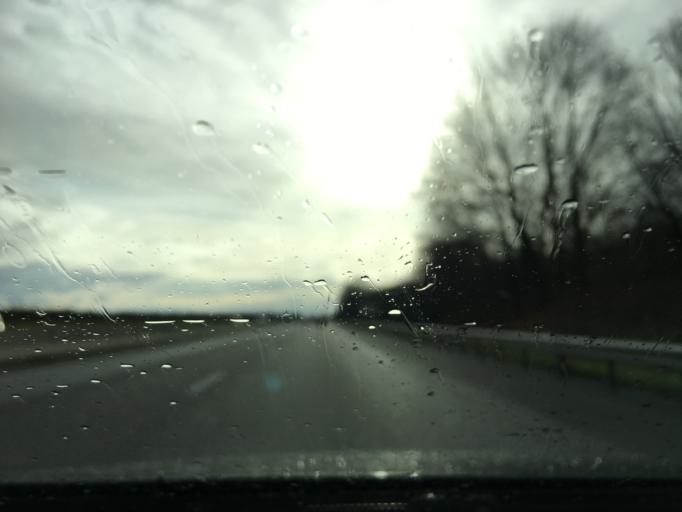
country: FR
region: Alsace
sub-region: Departement du Haut-Rhin
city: Rixheim
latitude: 47.7534
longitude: 7.4200
